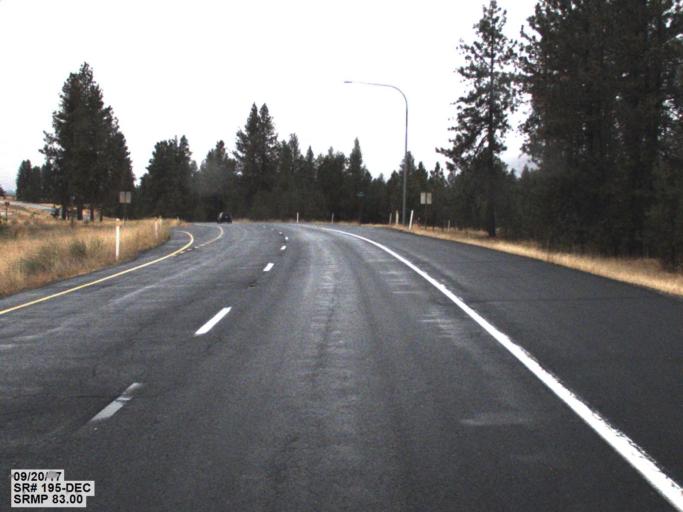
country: US
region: Washington
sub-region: Spokane County
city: Cheney
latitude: 47.4732
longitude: -117.4004
